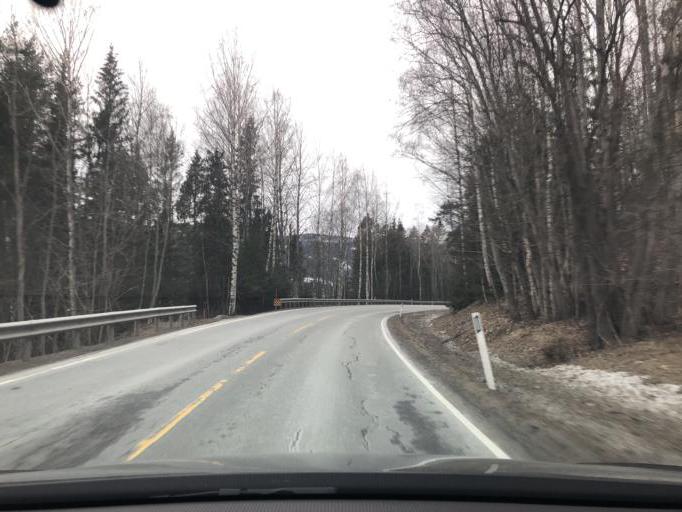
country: NO
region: Buskerud
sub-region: Ringerike
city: Honefoss
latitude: 60.4447
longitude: 10.0764
